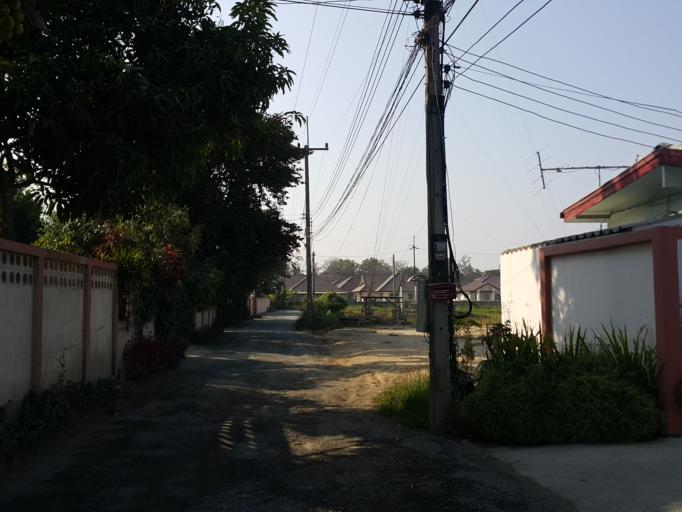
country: TH
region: Chiang Mai
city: San Kamphaeng
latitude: 18.7838
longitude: 99.0923
